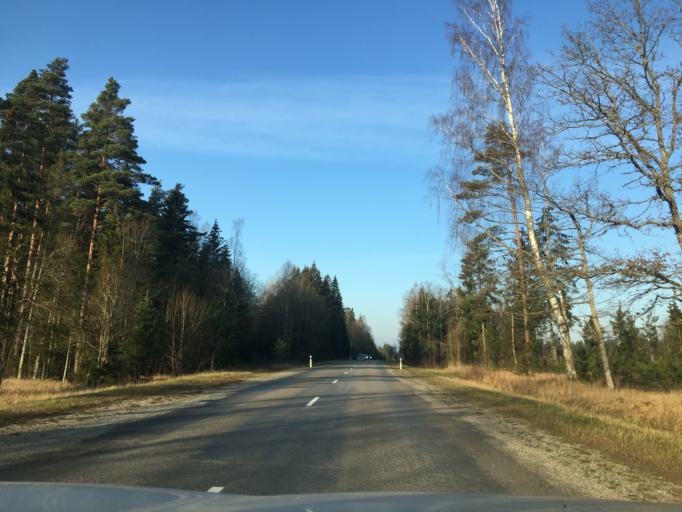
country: LV
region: Kuldigas Rajons
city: Kuldiga
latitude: 57.0458
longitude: 21.8248
